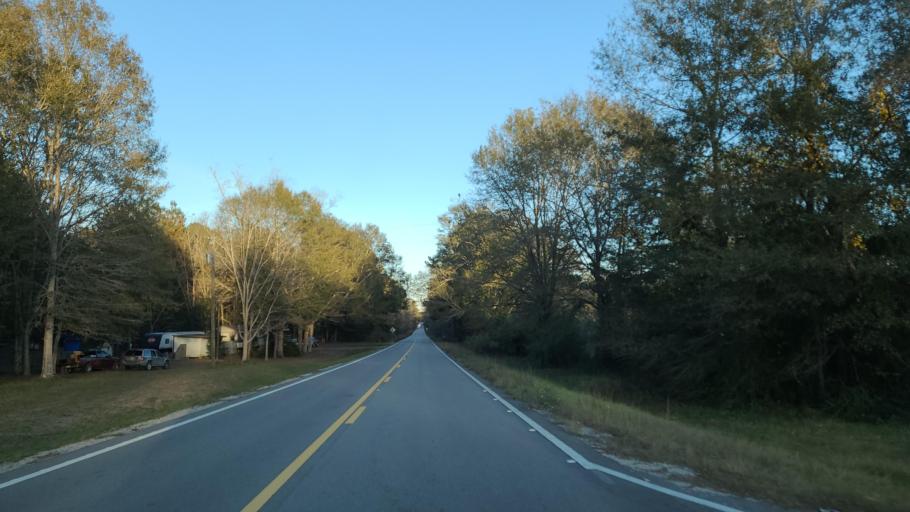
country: US
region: Mississippi
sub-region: Lamar County
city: Lumberton
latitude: 31.0005
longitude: -89.3407
